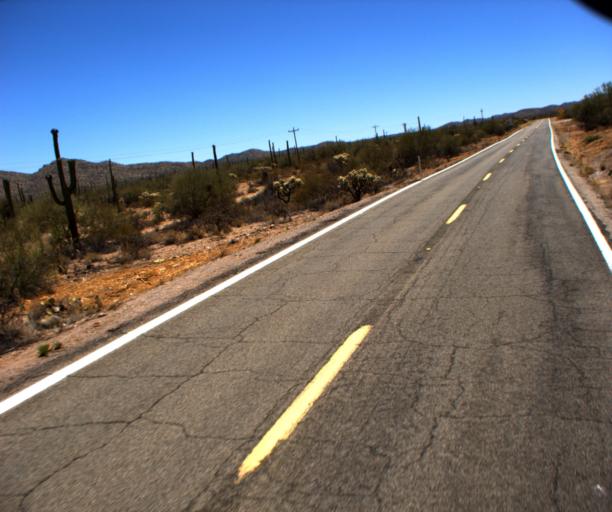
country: US
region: Arizona
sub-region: Pima County
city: Sells
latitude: 32.1769
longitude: -112.2649
